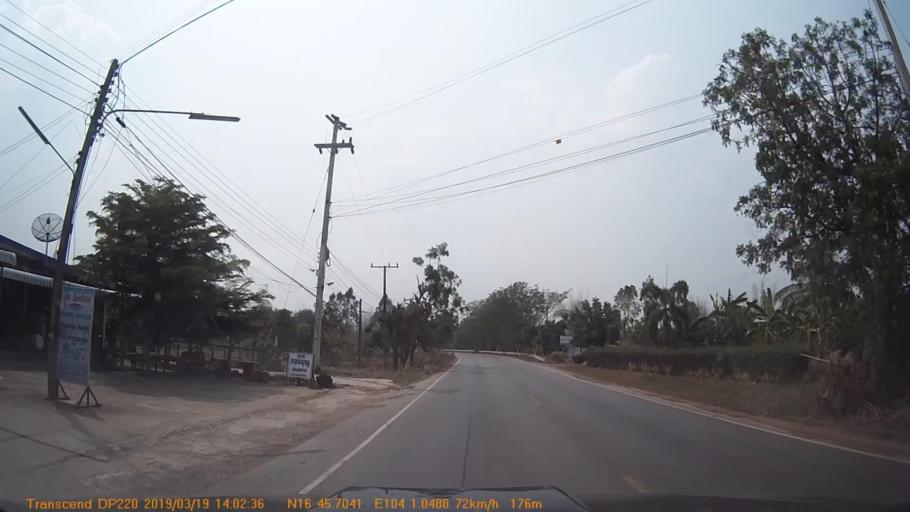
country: TH
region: Kalasin
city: Na Khu
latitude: 16.7619
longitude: 104.0170
